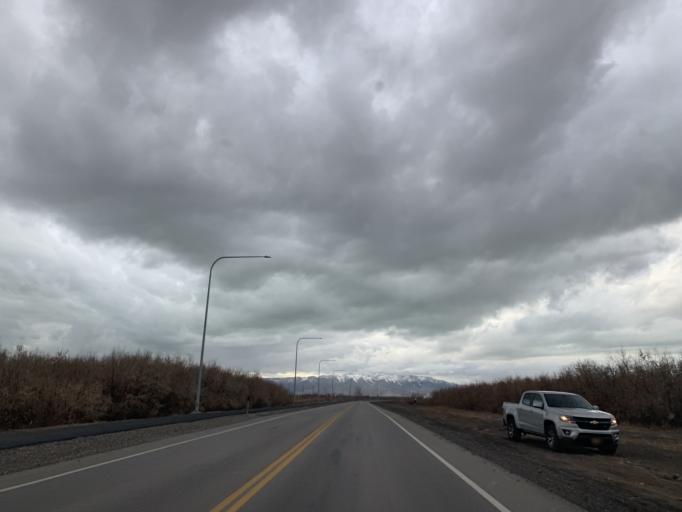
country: US
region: Utah
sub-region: Utah County
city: Provo
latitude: 40.2113
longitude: -111.6830
